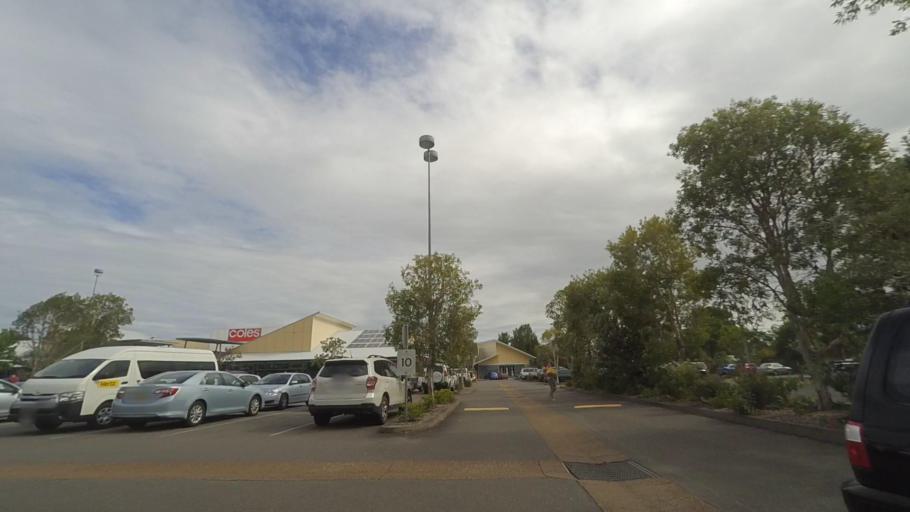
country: AU
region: New South Wales
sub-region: Great Lakes
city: Hawks Nest
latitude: -32.6516
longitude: 152.1498
